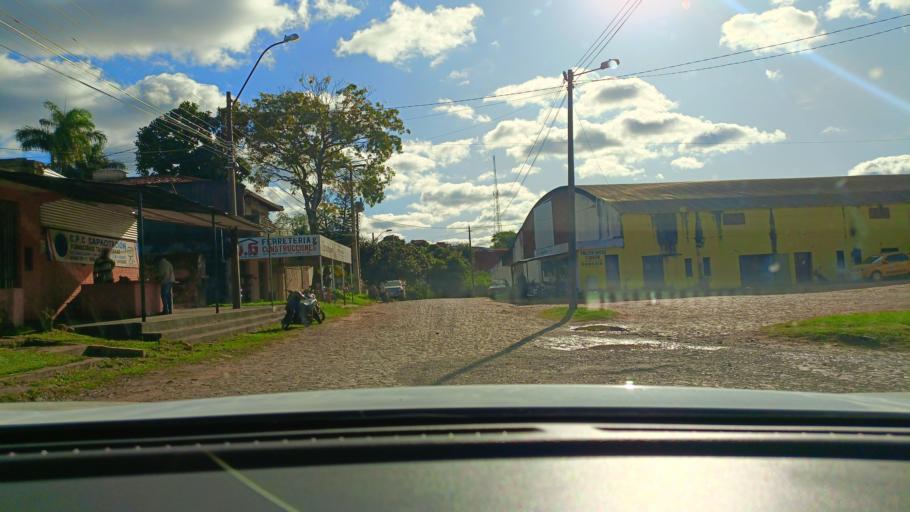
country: PY
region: San Pedro
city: Guayaybi
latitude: -24.6659
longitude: -56.4399
